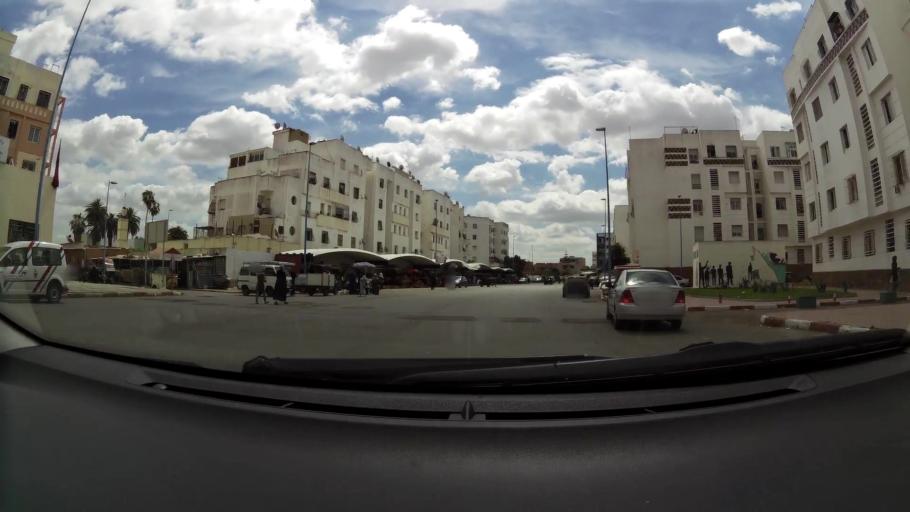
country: MA
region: Grand Casablanca
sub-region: Casablanca
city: Casablanca
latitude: 33.6109
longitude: -7.5439
